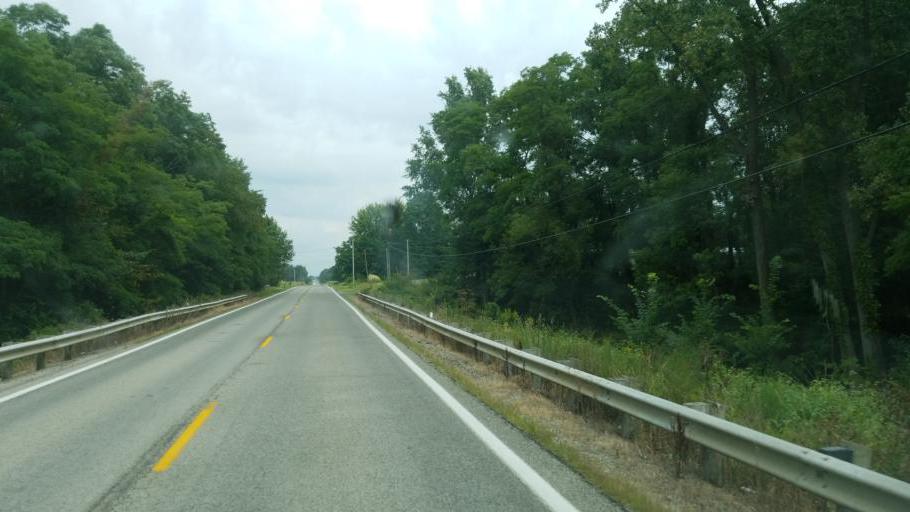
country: US
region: Ohio
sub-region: Crawford County
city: Galion
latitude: 40.6725
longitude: -82.7655
